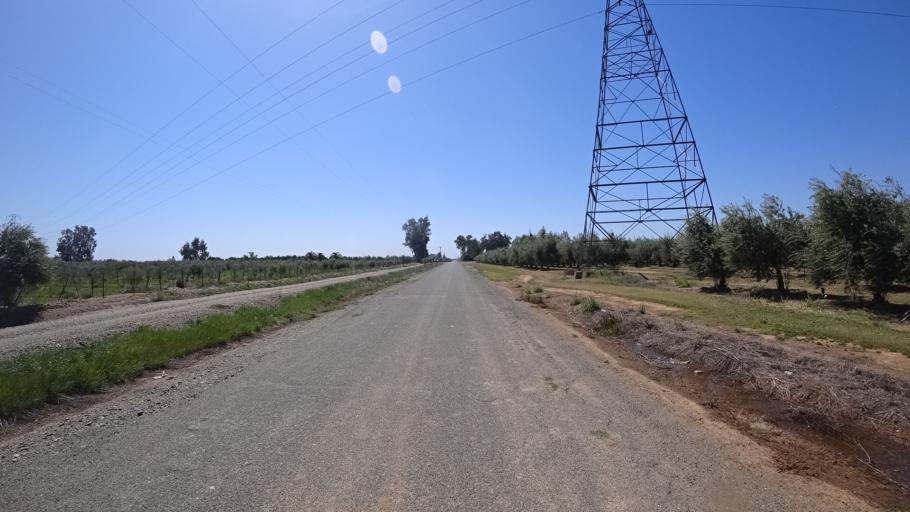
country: US
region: California
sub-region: Glenn County
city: Orland
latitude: 39.7942
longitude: -122.1691
